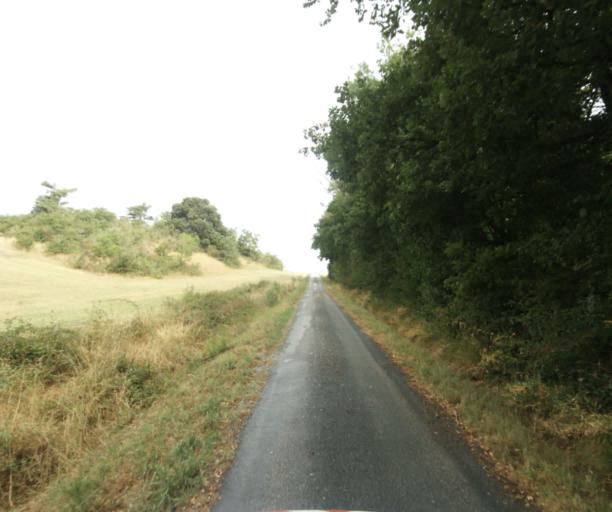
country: FR
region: Midi-Pyrenees
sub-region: Departement de la Haute-Garonne
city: Revel
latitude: 43.4251
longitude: 1.9727
